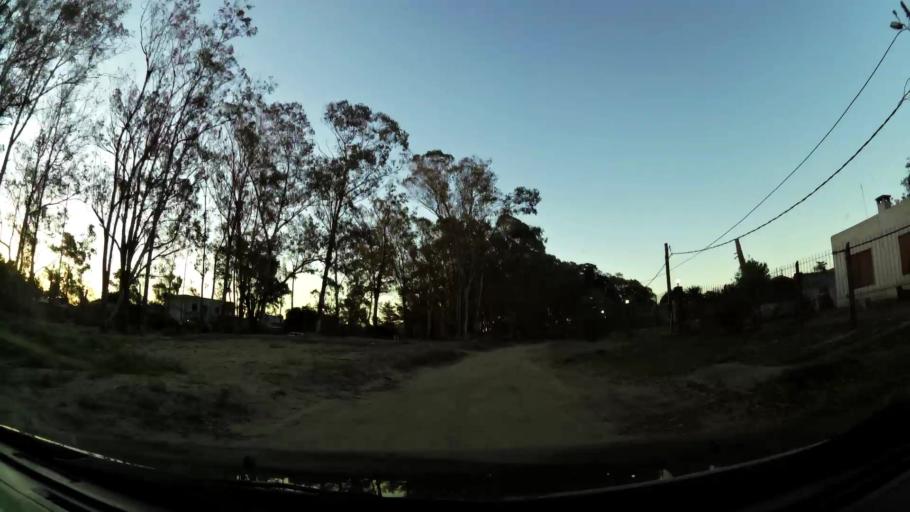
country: UY
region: Canelones
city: Barra de Carrasco
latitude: -34.8305
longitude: -55.9594
